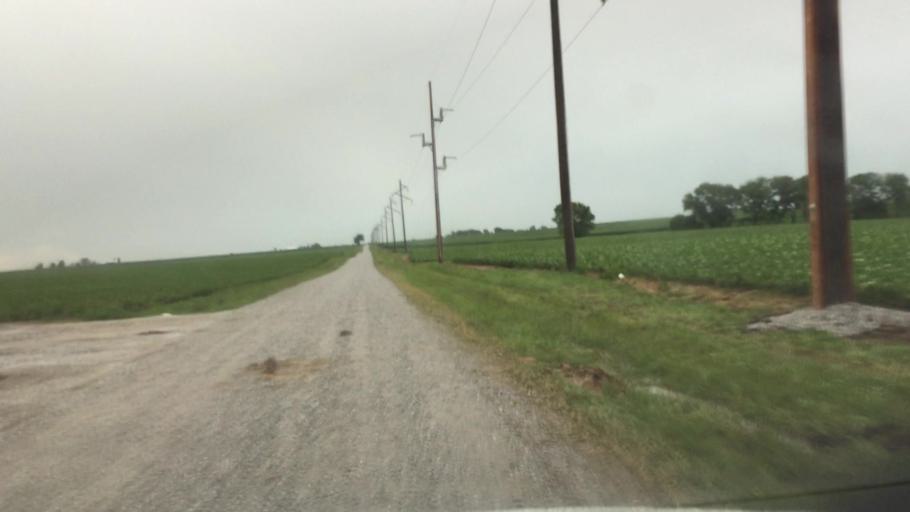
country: US
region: Illinois
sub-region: Hancock County
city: Hamilton
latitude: 40.4248
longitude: -91.2706
